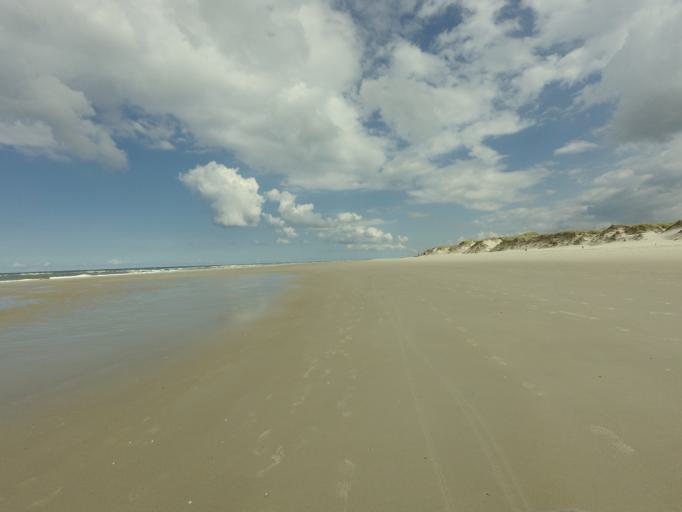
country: NL
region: Friesland
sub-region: Gemeente Terschelling
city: West-Terschelling
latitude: 53.3994
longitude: 5.2247
